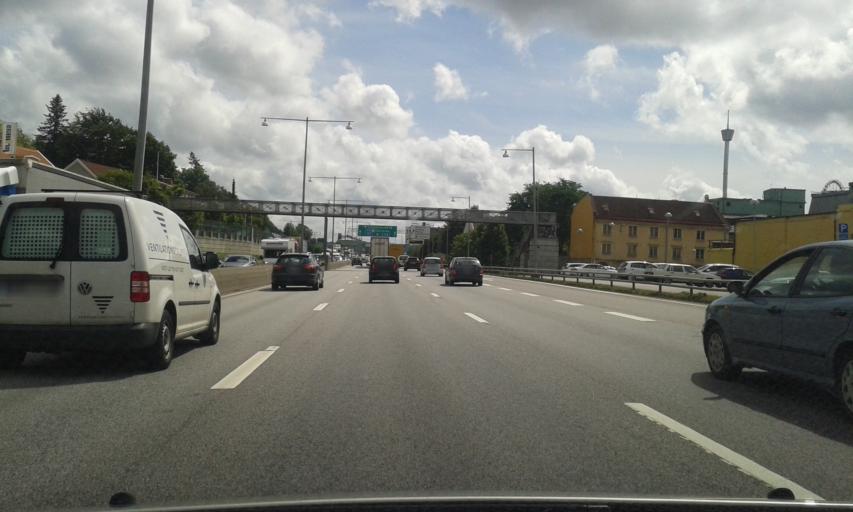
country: SE
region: Vaestra Goetaland
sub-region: Goteborg
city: Goeteborg
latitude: 57.7018
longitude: 11.9945
